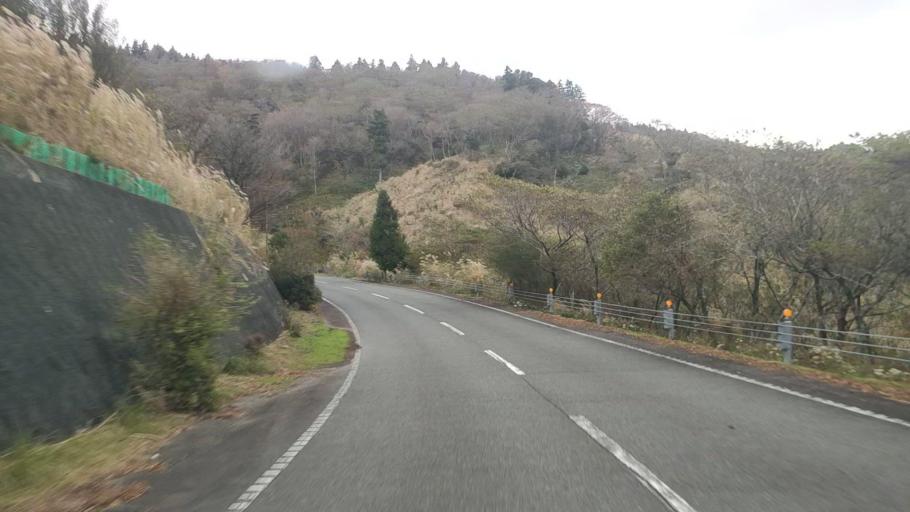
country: JP
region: Shizuoka
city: Heda
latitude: 34.9068
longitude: 138.8472
